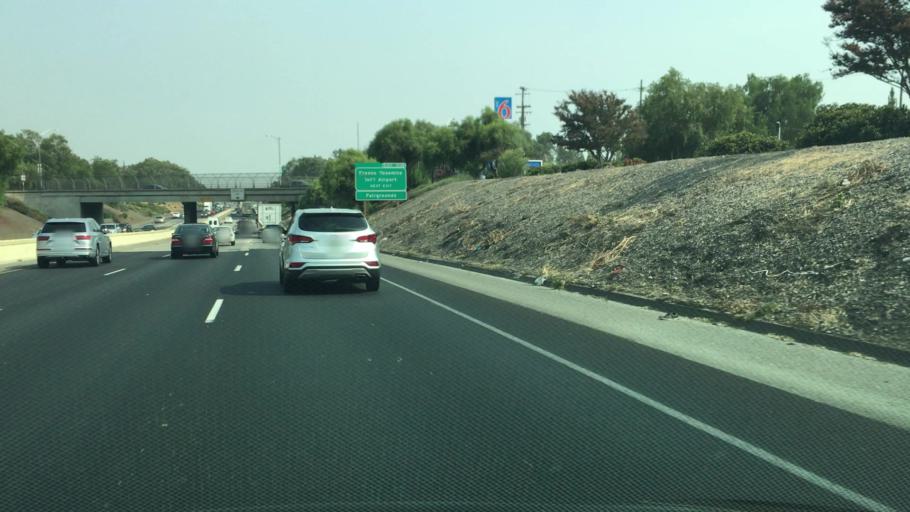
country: US
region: California
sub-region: Fresno County
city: West Park
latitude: 36.7514
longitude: -119.8260
